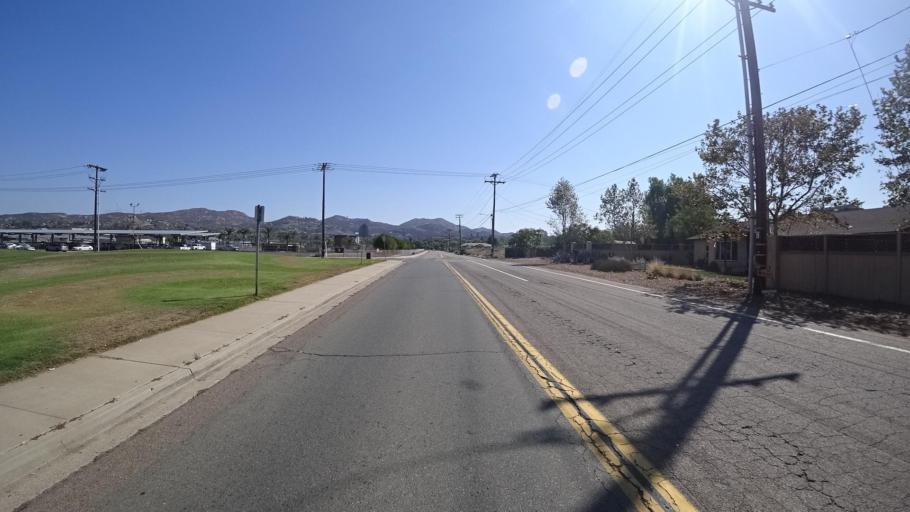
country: US
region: California
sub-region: San Diego County
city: Granite Hills
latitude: 32.7964
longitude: -116.9187
